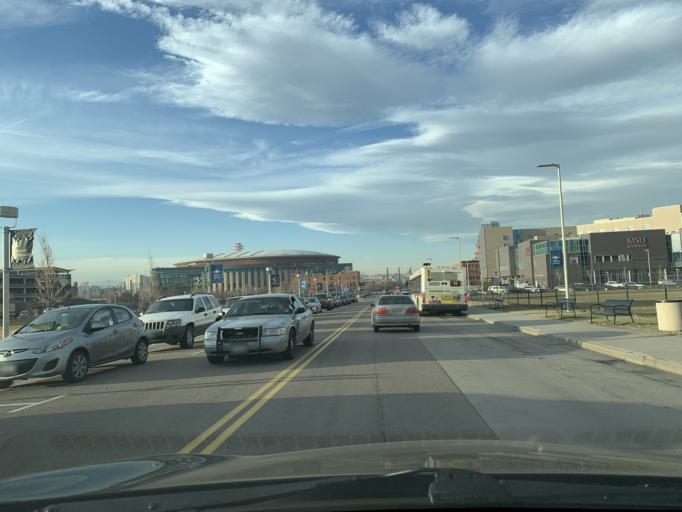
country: US
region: Colorado
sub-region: Denver County
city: Denver
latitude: 39.7456
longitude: -105.0038
